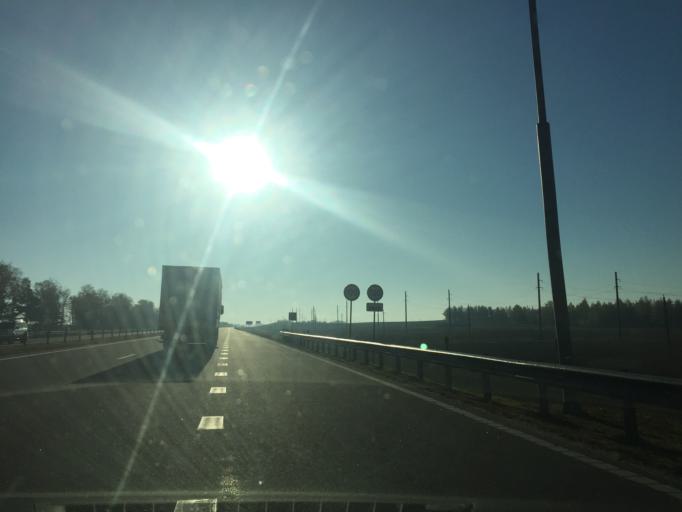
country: BY
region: Minsk
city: Luhavaya Slabada
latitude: 53.7791
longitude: 27.8463
